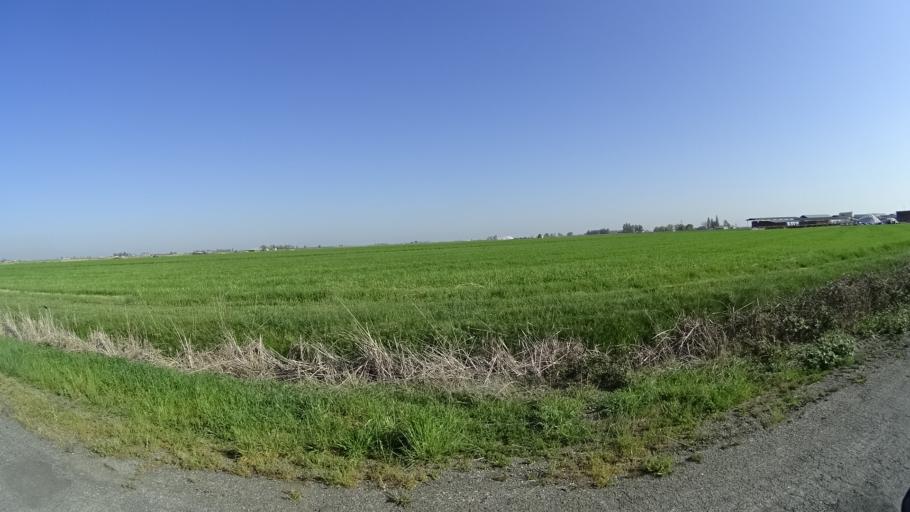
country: US
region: California
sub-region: Glenn County
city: Willows
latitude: 39.5726
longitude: -122.0718
